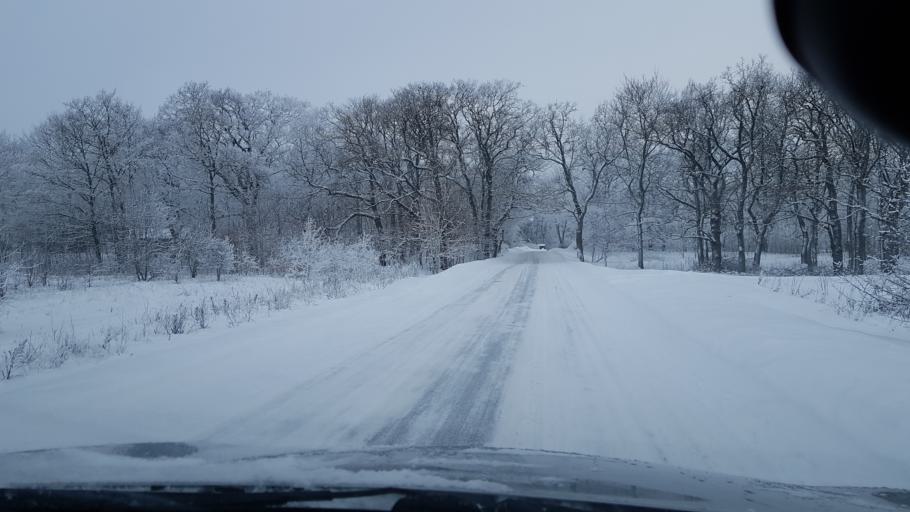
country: EE
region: Harju
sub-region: Keila linn
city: Keila
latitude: 59.3376
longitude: 24.3931
